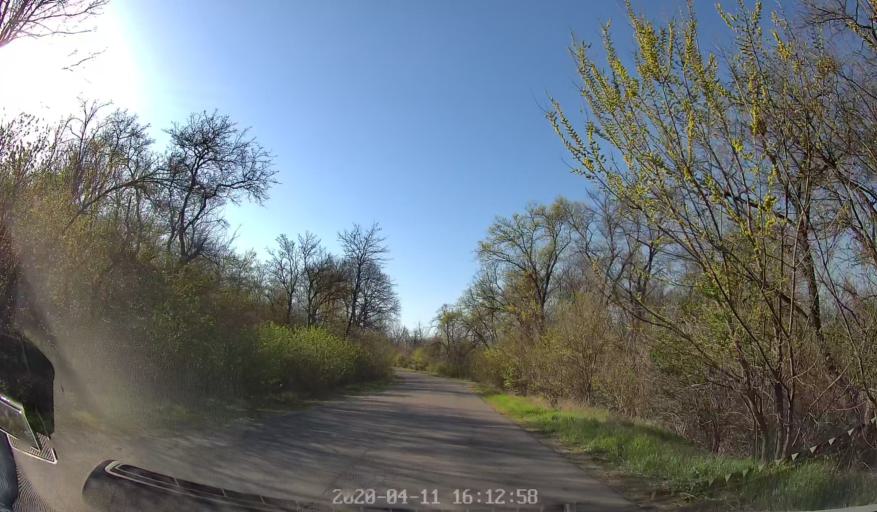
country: MD
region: Chisinau
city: Vadul lui Voda
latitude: 47.0710
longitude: 29.1167
